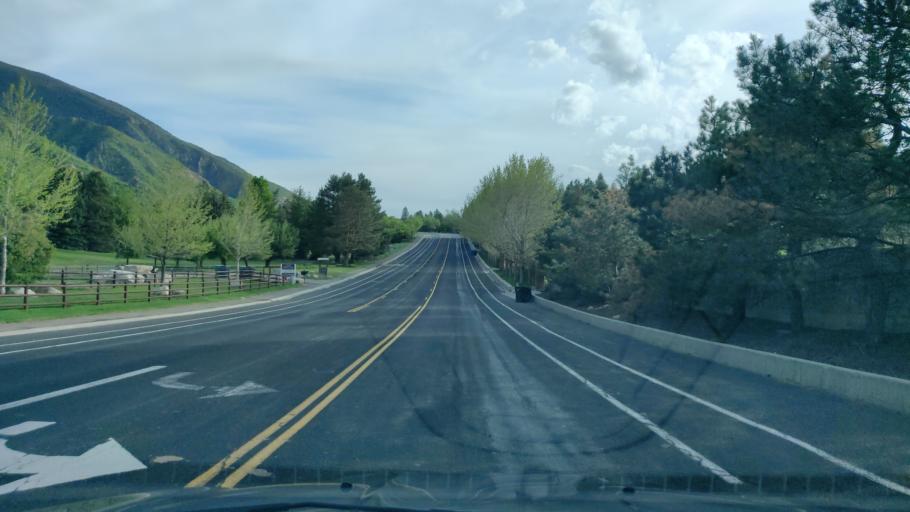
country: US
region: Utah
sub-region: Salt Lake County
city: Granite
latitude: 40.5571
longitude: -111.8010
